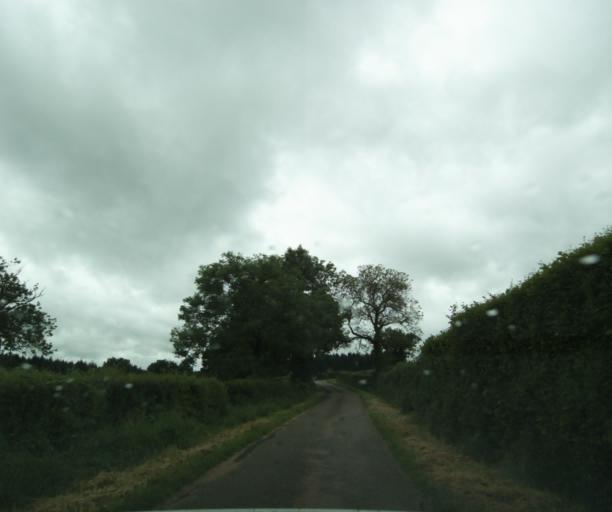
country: FR
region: Bourgogne
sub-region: Departement de Saone-et-Loire
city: Charolles
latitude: 46.4591
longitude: 4.4168
